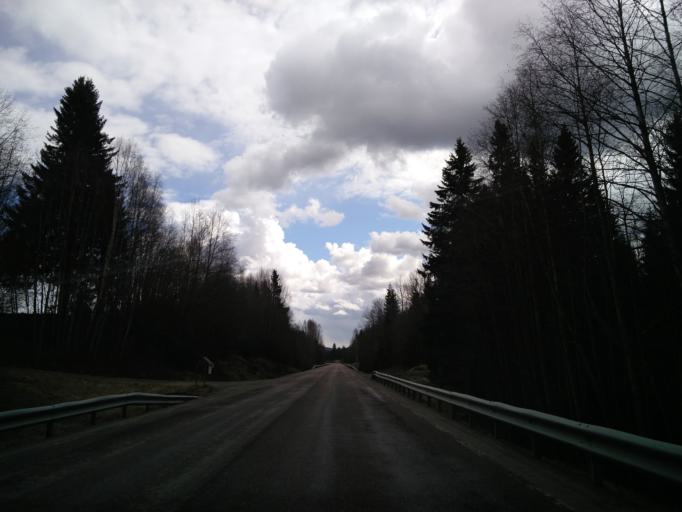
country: SE
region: Vaesternorrland
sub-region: Sundsvalls Kommun
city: Matfors
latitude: 62.4846
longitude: 17.1305
